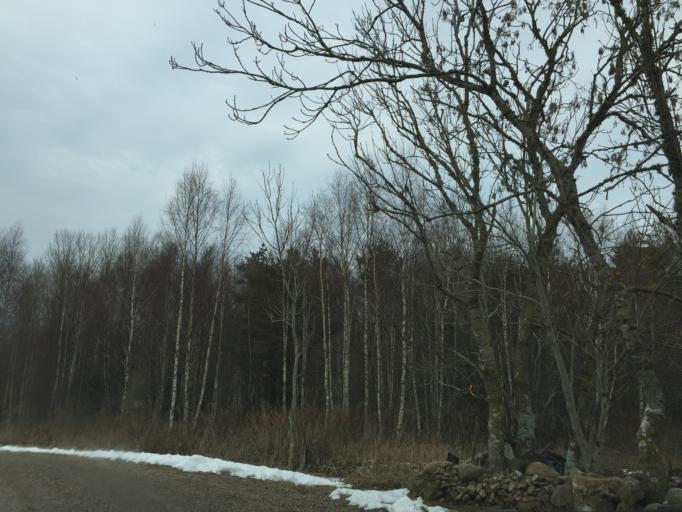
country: EE
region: Saare
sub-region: Kuressaare linn
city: Kuressaare
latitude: 58.4410
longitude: 22.1419
